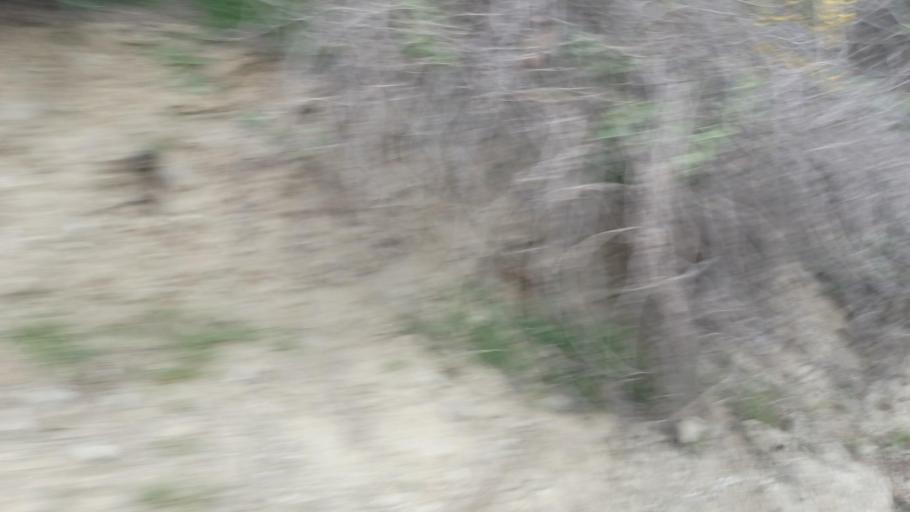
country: CY
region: Limassol
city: Pelendri
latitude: 34.8626
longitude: 33.0907
